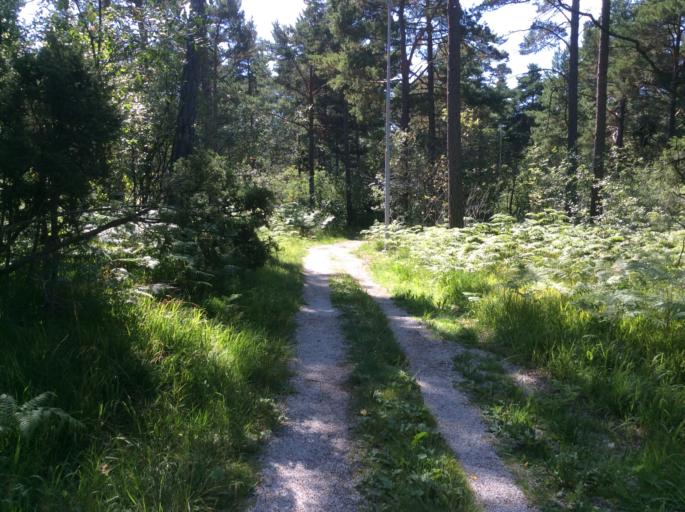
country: SE
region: Gotland
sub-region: Gotland
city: Vibble
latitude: 57.6017
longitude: 18.2726
